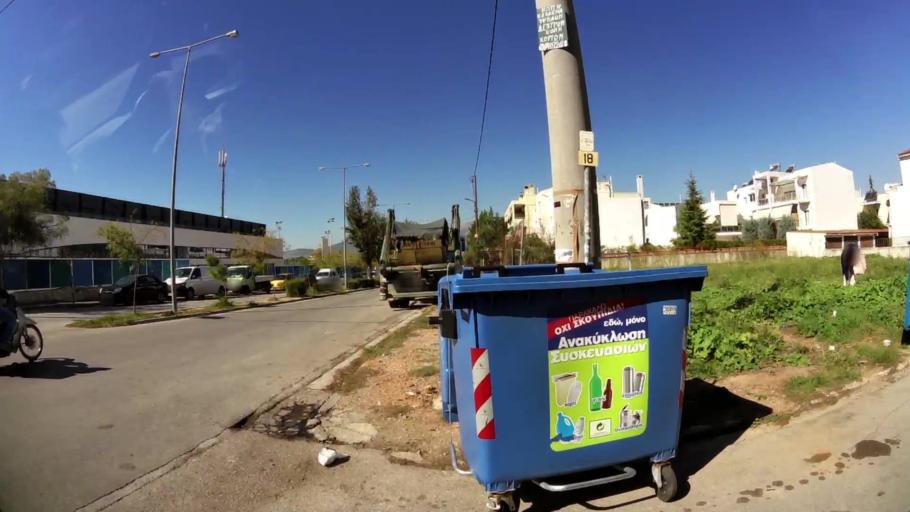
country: GR
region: Attica
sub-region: Nomarchia Athinas
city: Nea Erythraia
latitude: 38.0972
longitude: 23.8070
